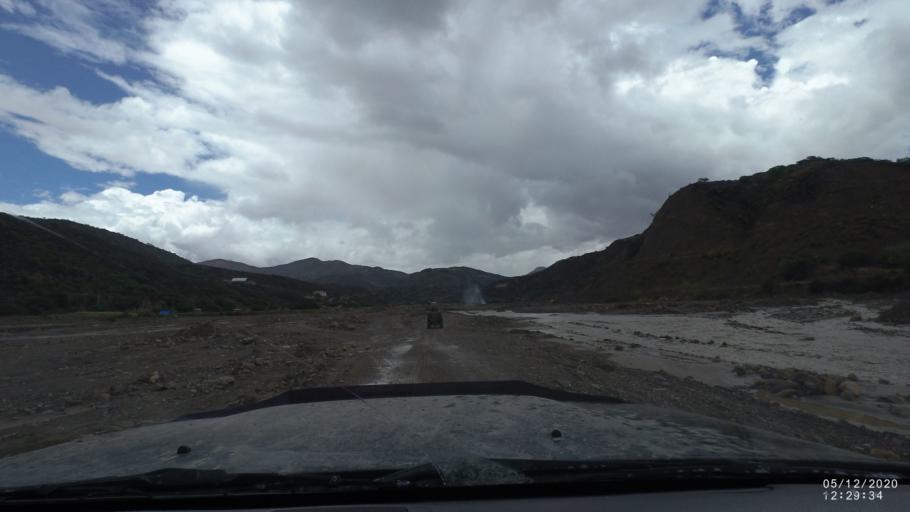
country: BO
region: Cochabamba
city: Sipe Sipe
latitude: -17.5466
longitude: -66.4160
